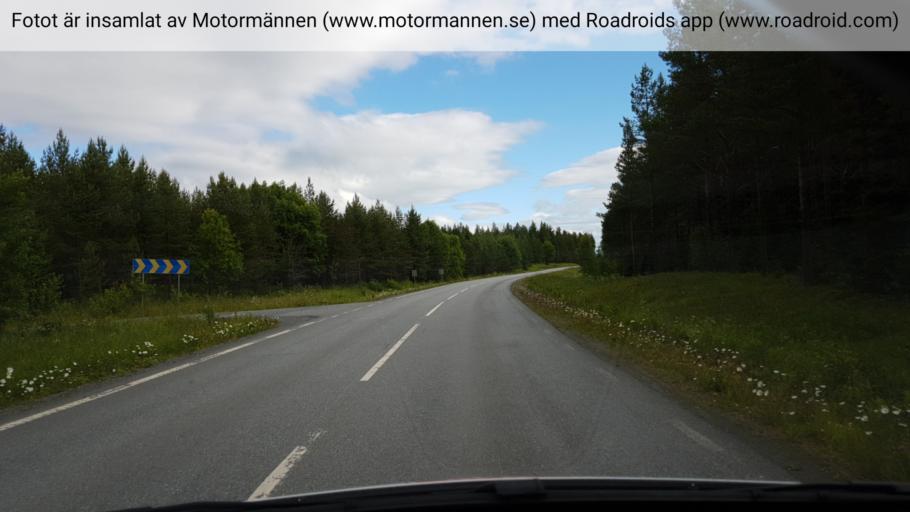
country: SE
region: Jaemtland
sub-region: Krokoms Kommun
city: Krokom
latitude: 63.2542
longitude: 14.4280
